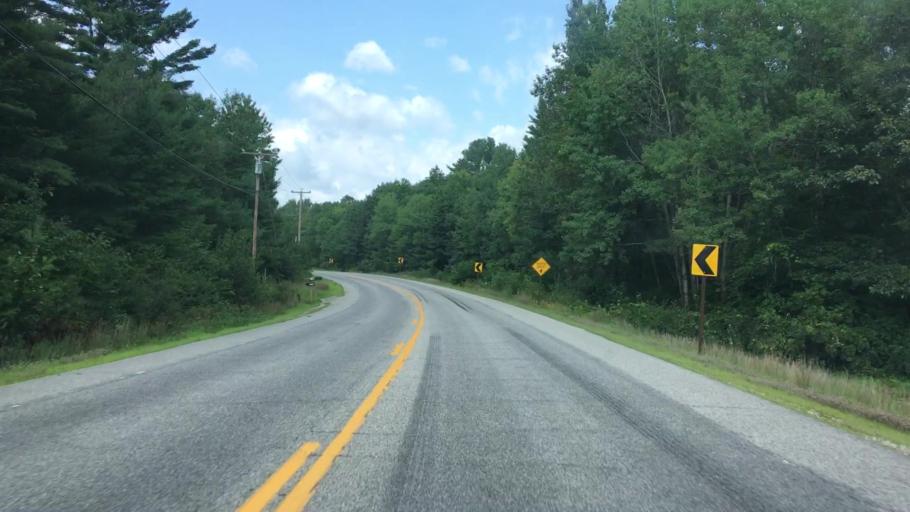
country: US
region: Maine
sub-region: Androscoggin County
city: Minot
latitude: 44.0300
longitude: -70.3364
